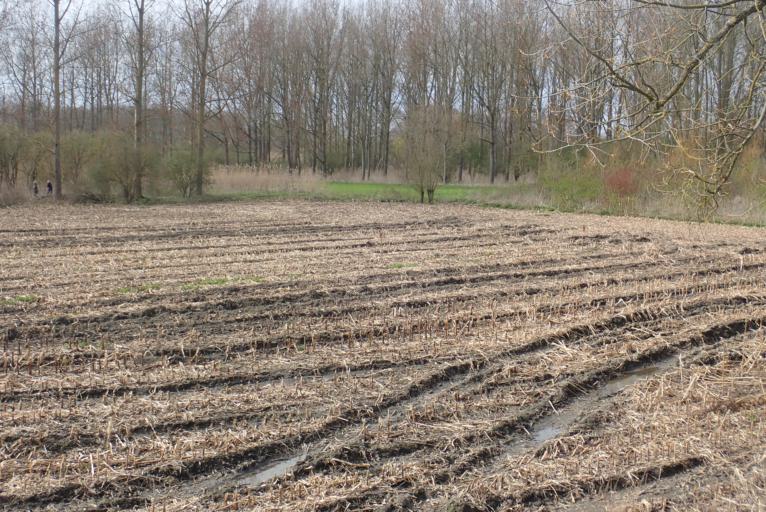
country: BE
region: Flanders
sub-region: Provincie Oost-Vlaanderen
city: Hamme
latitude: 51.1030
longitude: 4.1288
